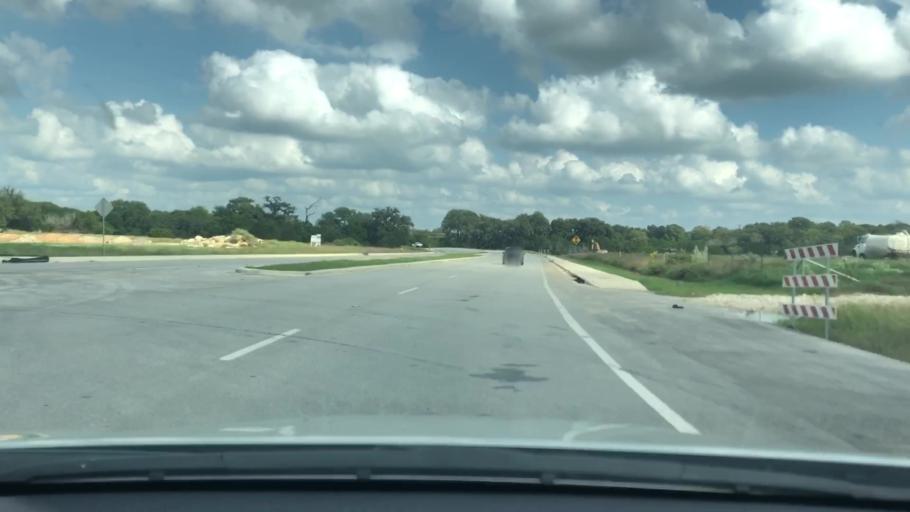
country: US
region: Texas
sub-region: Kendall County
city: Boerne
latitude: 29.7765
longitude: -98.7216
